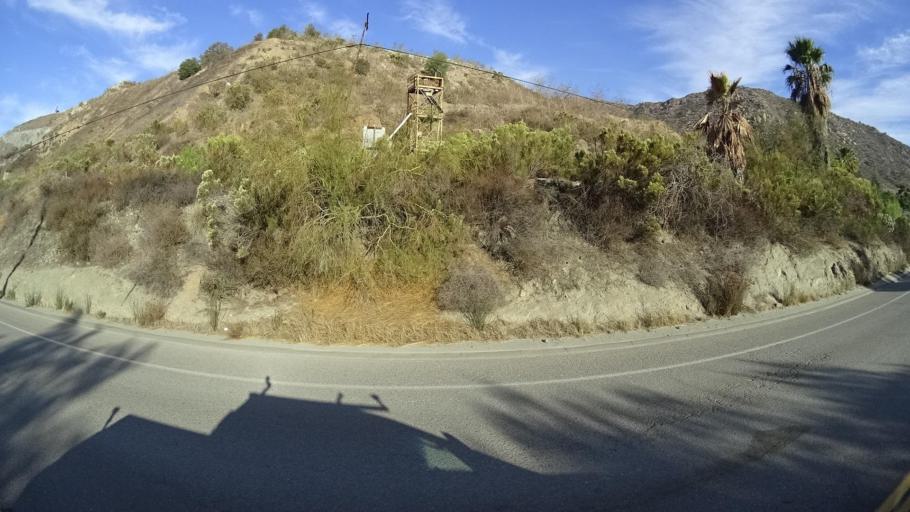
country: US
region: California
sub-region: San Diego County
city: Granite Hills
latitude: 32.7622
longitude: -116.8903
